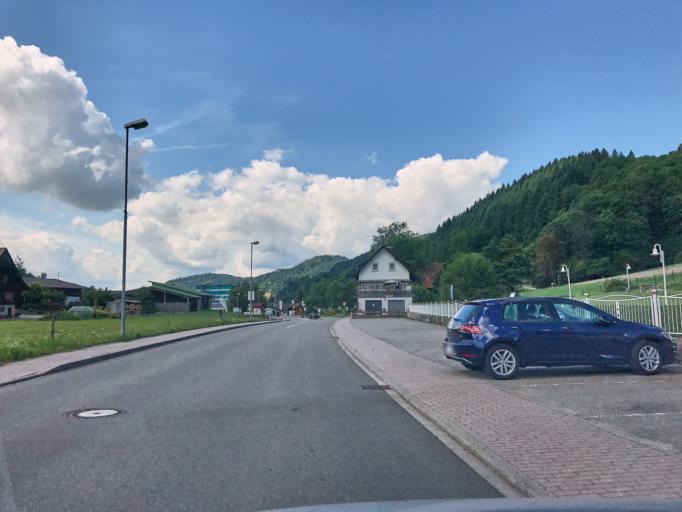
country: DE
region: Baden-Wuerttemberg
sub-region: Freiburg Region
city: Nordrach
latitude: 48.3965
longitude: 8.0775
